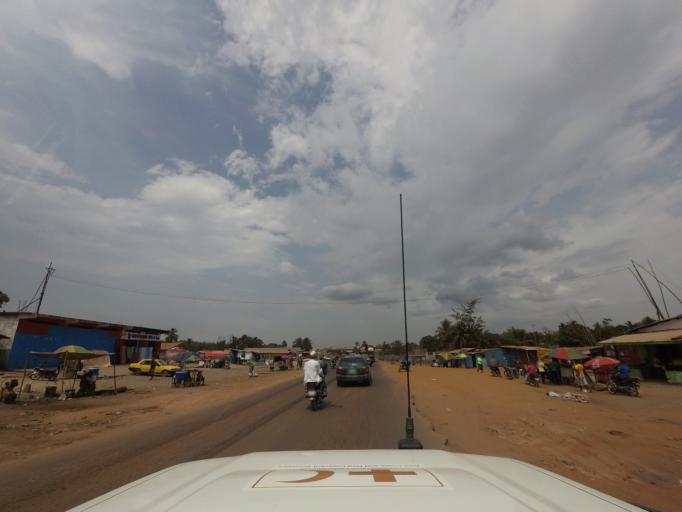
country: LR
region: Montserrado
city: Monrovia
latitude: 6.2974
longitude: -10.6820
